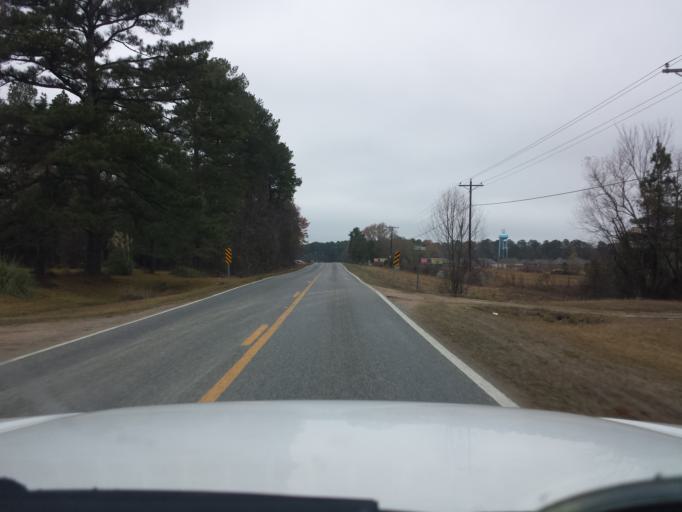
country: US
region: Mississippi
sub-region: Madison County
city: Canton
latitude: 32.4921
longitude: -89.9227
